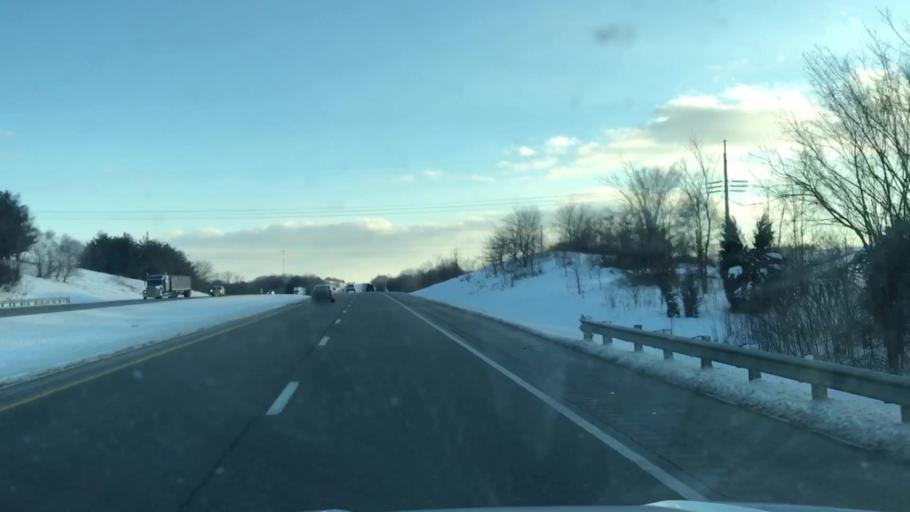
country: US
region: Missouri
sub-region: Andrew County
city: Country Club Village
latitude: 39.8457
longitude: -94.8054
